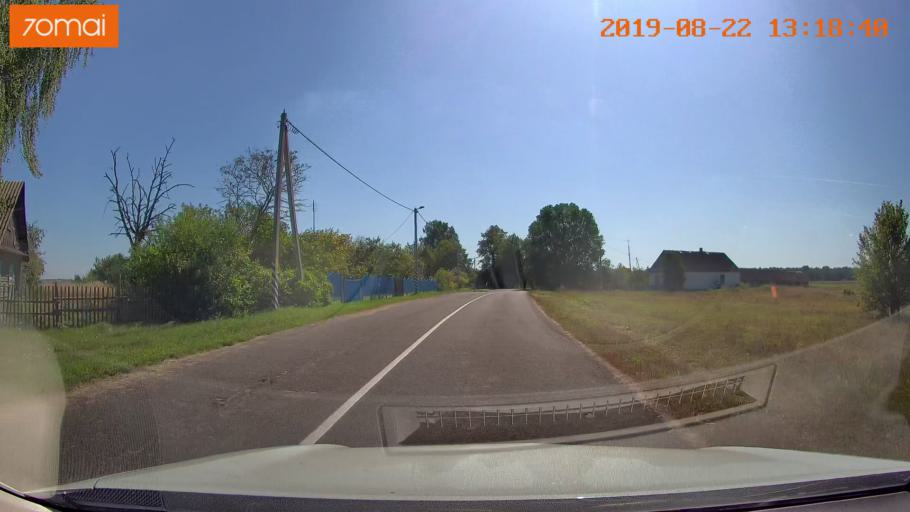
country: BY
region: Minsk
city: Urechcha
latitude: 53.2393
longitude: 27.9421
